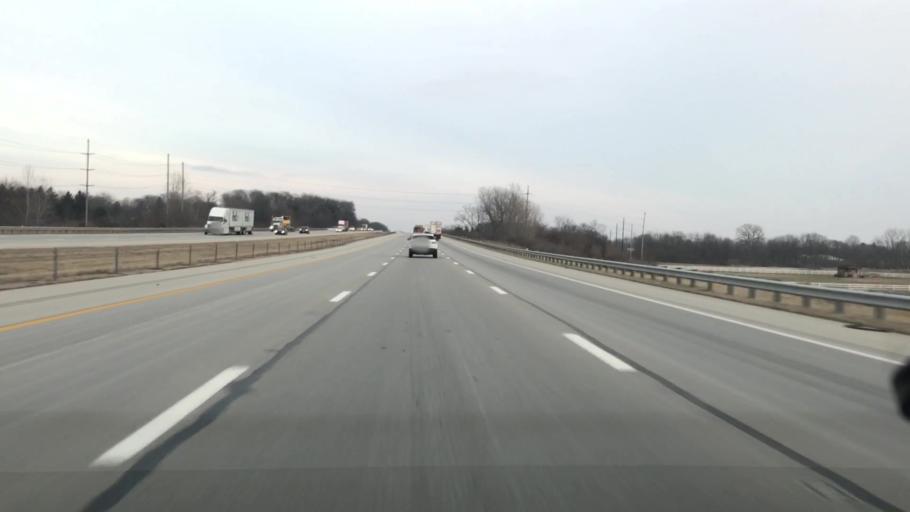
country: US
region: Ohio
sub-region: Clark County
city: Springfield
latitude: 39.8896
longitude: -83.7699
